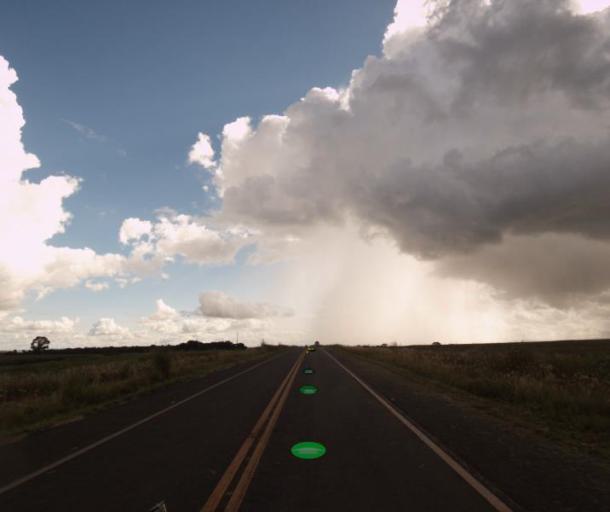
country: BR
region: Goias
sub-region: Itaberai
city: Itaberai
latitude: -15.9898
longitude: -49.7207
